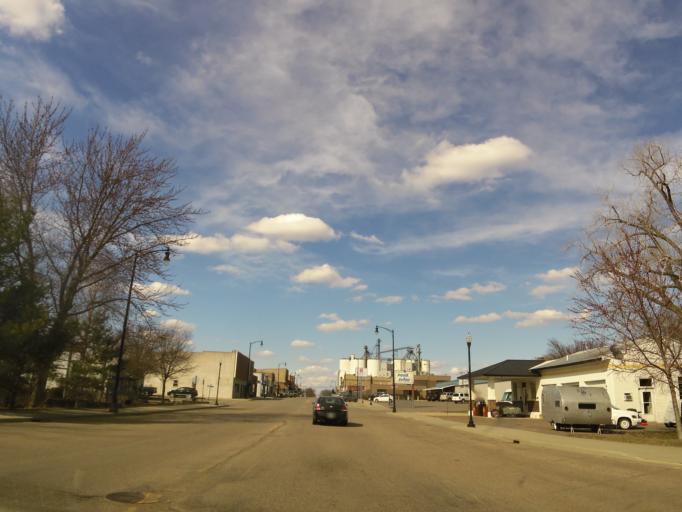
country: US
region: Minnesota
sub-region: Lac qui Parle County
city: Dawson
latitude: 44.9272
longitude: -96.0547
